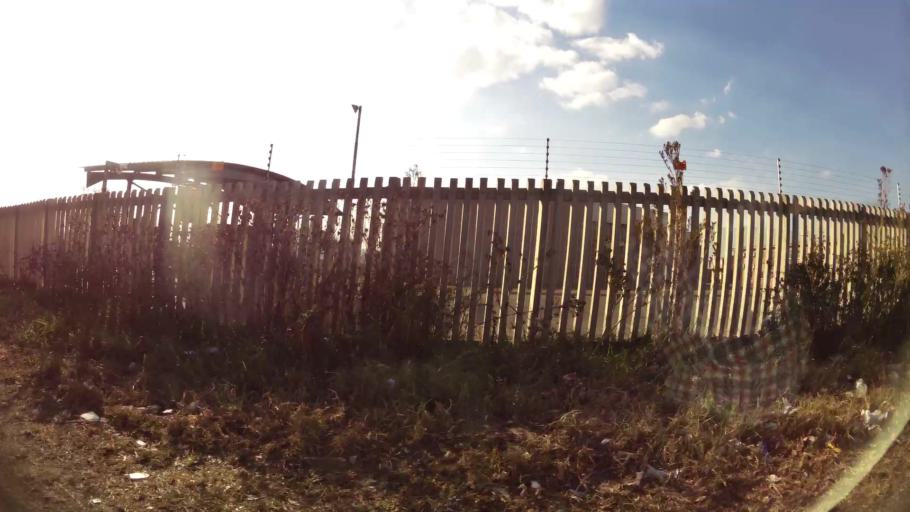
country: ZA
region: Gauteng
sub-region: City of Johannesburg Metropolitan Municipality
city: Soweto
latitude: -26.2627
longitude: 27.9153
